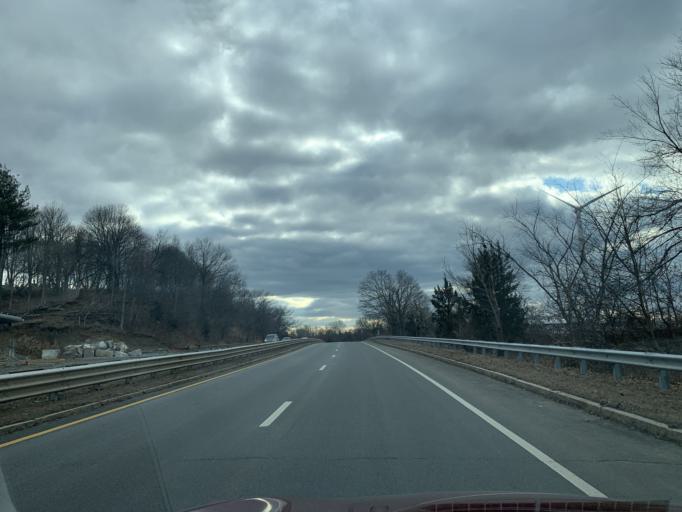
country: US
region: Massachusetts
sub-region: Essex County
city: Newburyport
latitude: 42.8052
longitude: -70.8789
